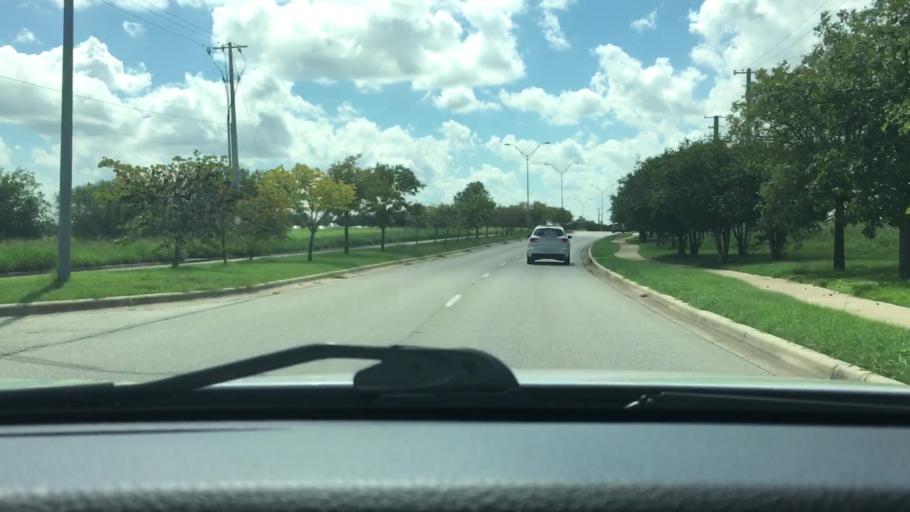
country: US
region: Texas
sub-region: Williamson County
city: Round Rock
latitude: 30.5665
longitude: -97.6867
